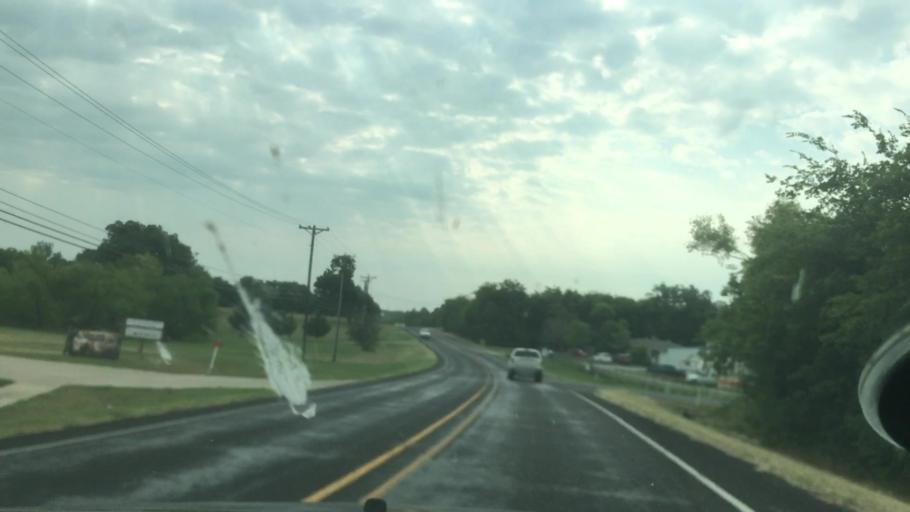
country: US
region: Texas
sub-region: Grayson County
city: Pottsboro
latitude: 33.7865
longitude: -96.6025
